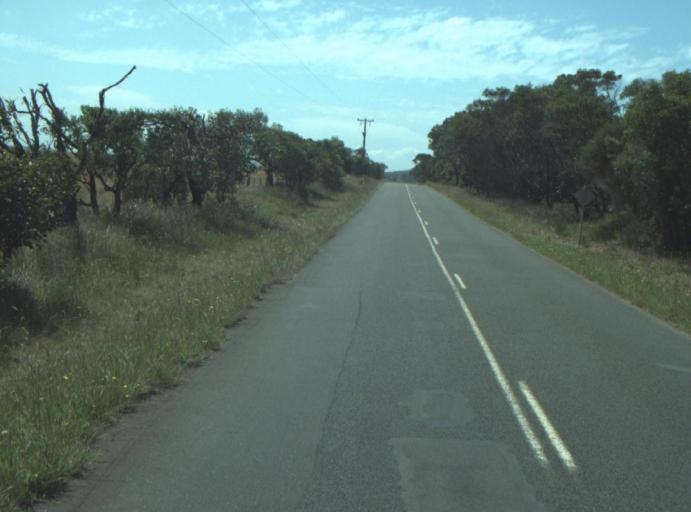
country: AU
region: Victoria
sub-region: Greater Geelong
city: Breakwater
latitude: -38.2912
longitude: 144.3670
